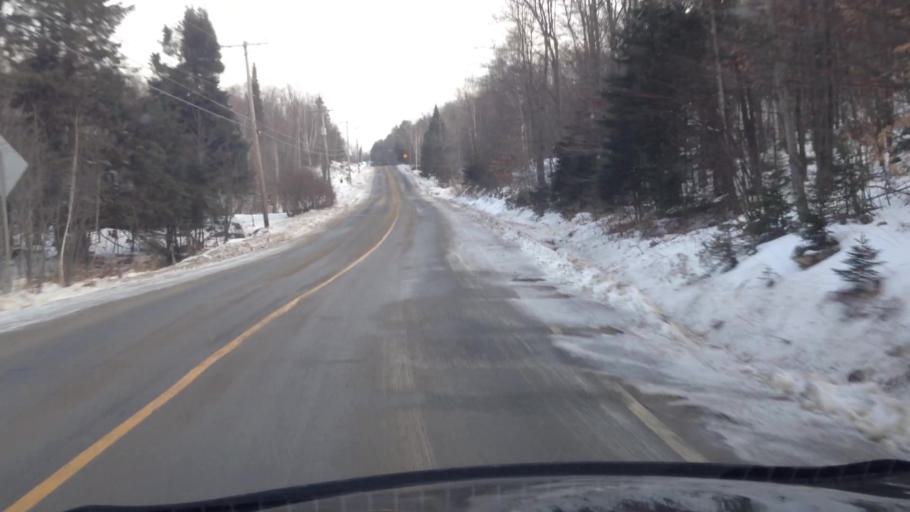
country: CA
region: Quebec
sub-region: Laurentides
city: Brownsburg-Chatham
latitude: 45.9220
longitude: -74.5064
